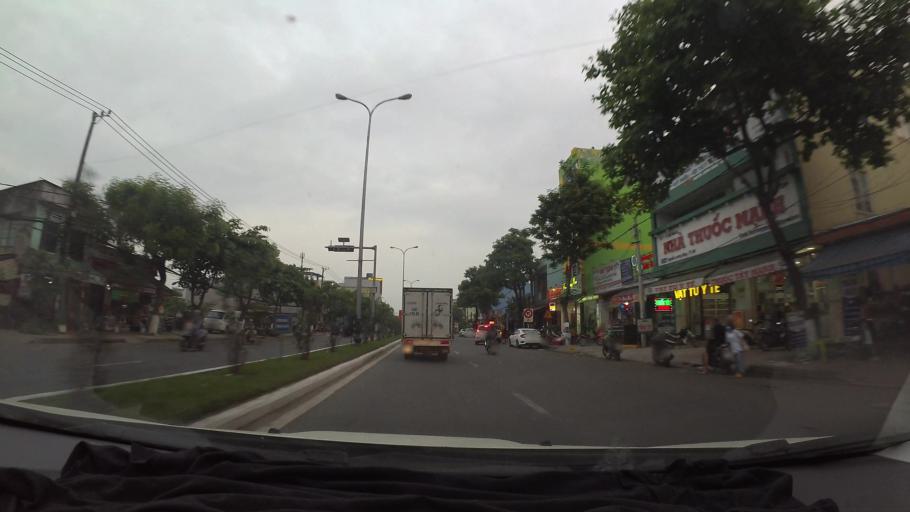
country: VN
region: Da Nang
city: Lien Chieu
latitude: 16.0829
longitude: 108.1459
